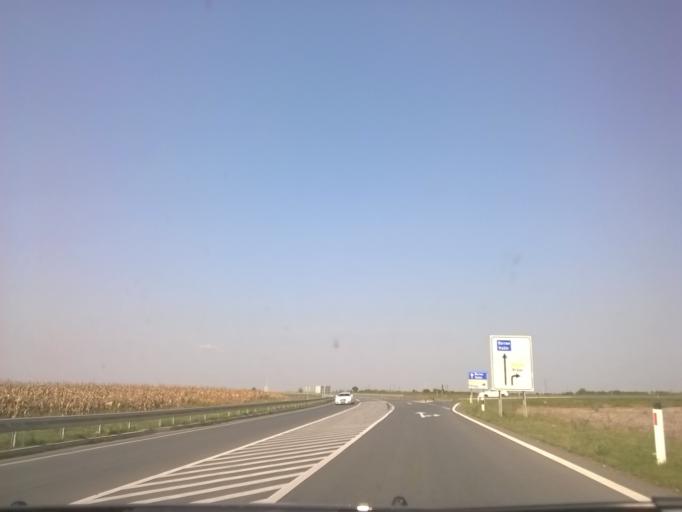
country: RS
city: Pavlis
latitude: 45.0940
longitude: 21.2602
